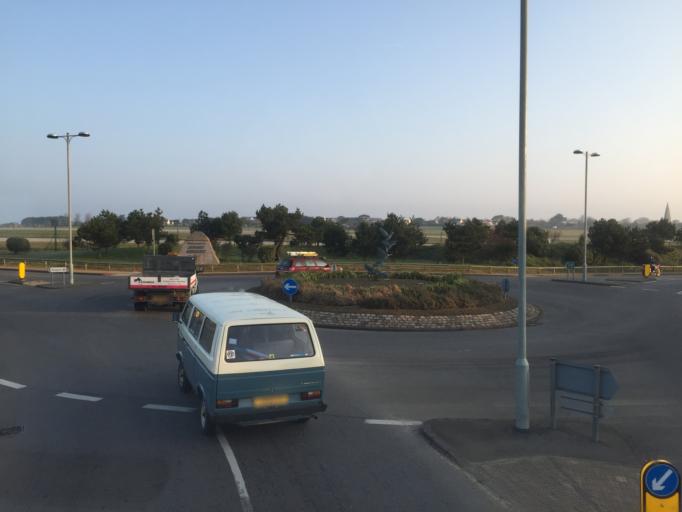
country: JE
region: St Helier
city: Saint Helier
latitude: 49.2059
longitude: -2.1899
